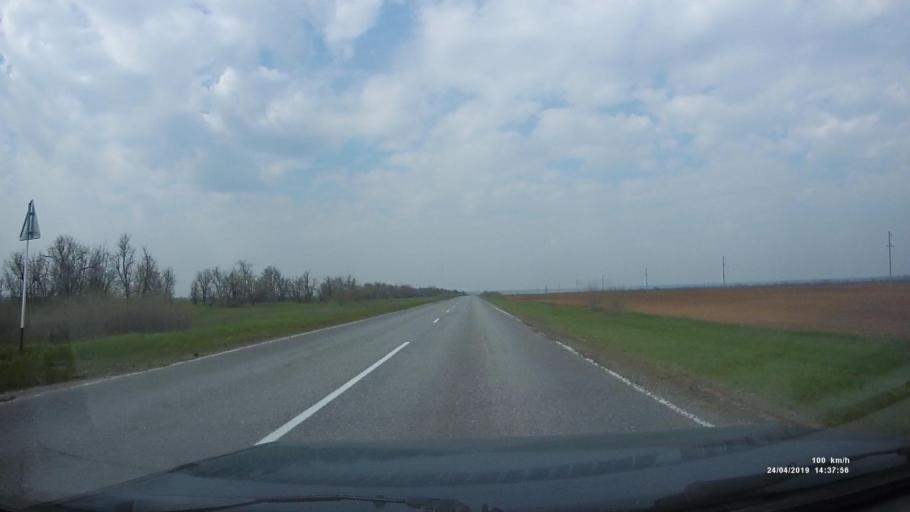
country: RU
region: Rostov
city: Remontnoye
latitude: 46.3935
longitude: 43.8864
